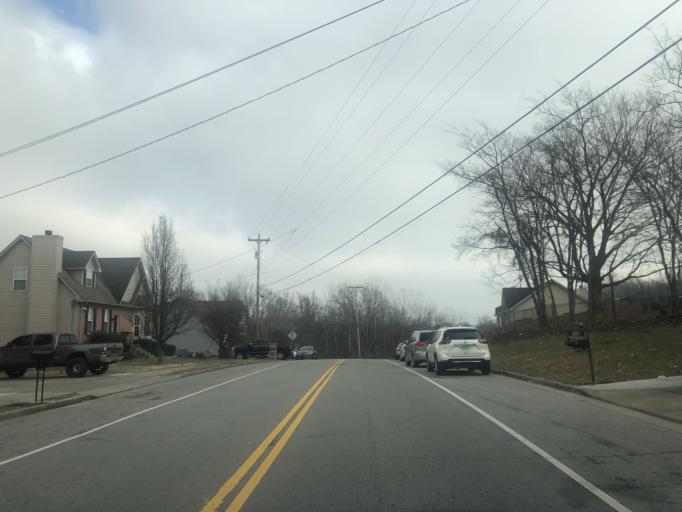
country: US
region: Tennessee
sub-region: Rutherford County
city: La Vergne
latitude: 36.0709
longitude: -86.6490
